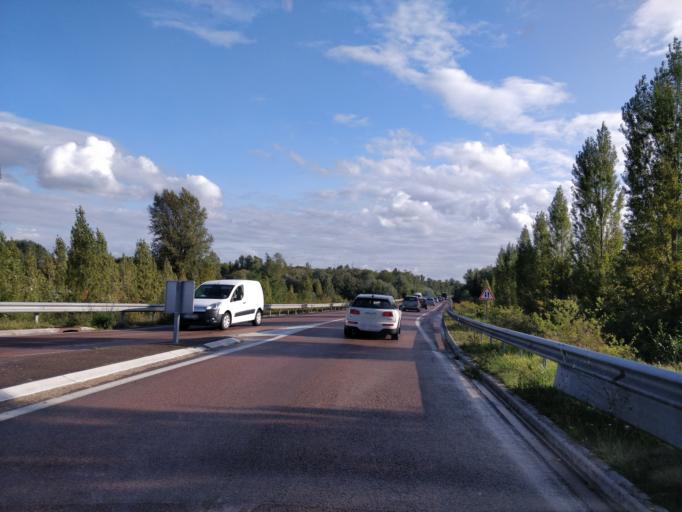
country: FR
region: Champagne-Ardenne
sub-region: Departement de l'Aube
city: Saint-Julien-les-Villas
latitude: 48.2620
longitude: 4.1159
